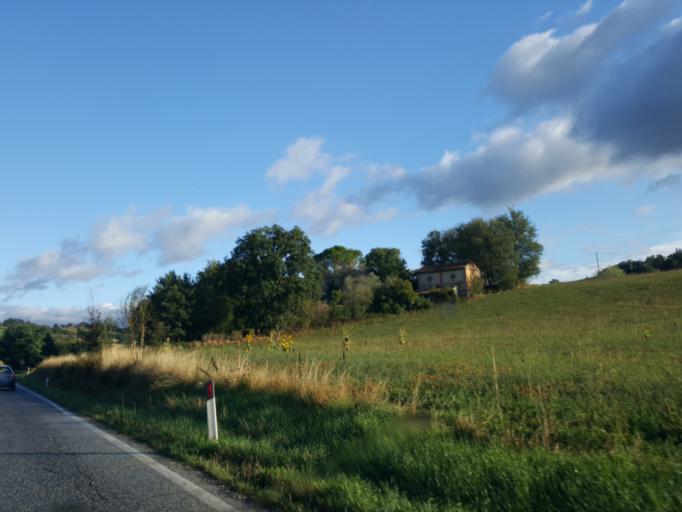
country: IT
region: The Marches
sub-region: Provincia di Macerata
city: Camerino
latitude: 43.1684
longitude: 13.0576
